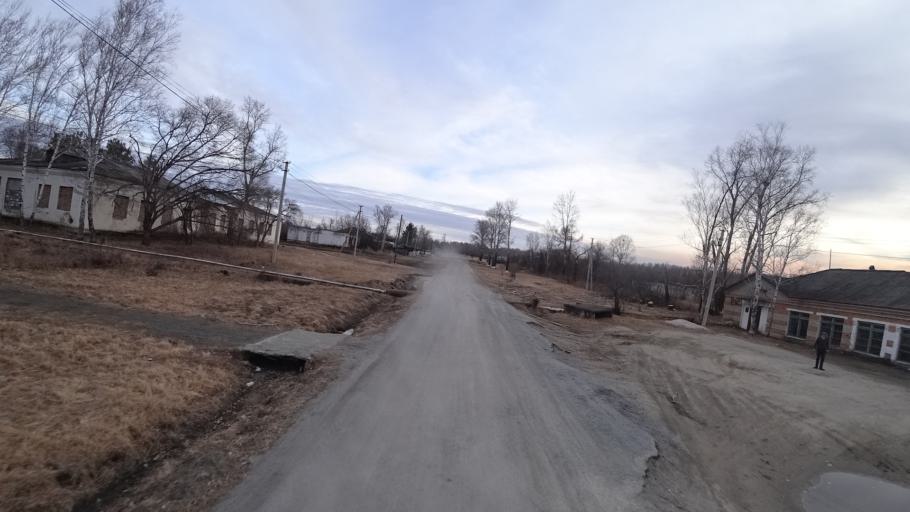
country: RU
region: Amur
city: Bureya
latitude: 50.0191
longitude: 129.7685
